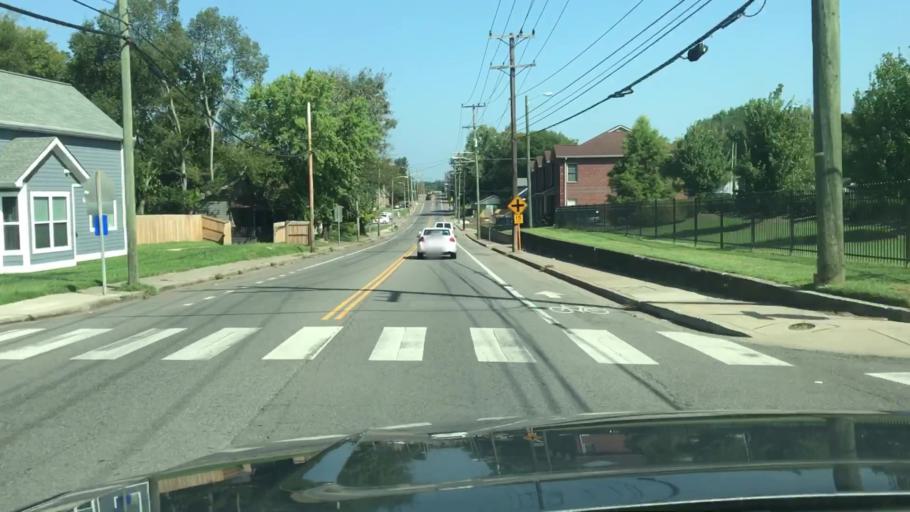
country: US
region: Tennessee
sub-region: Davidson County
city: Nashville
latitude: 36.1714
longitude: -86.8074
